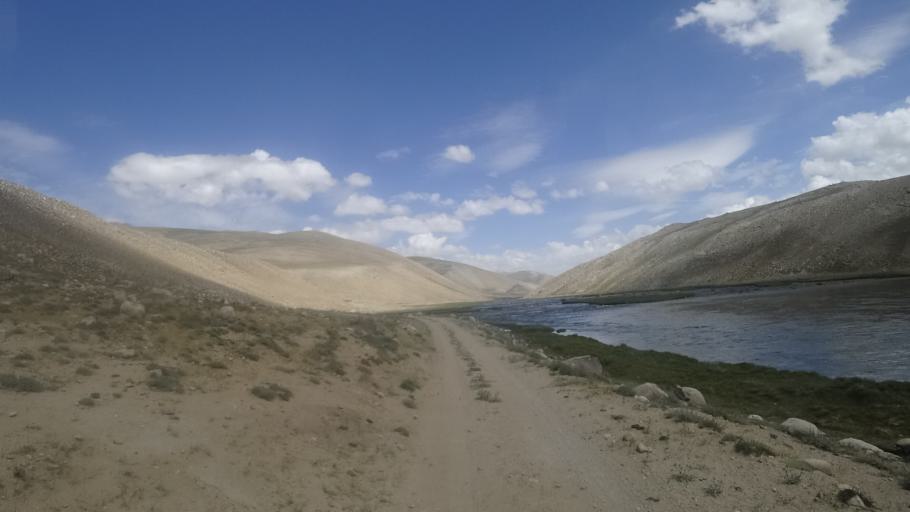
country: TJ
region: Gorno-Badakhshan
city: Murghob
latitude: 37.4737
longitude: 73.4493
